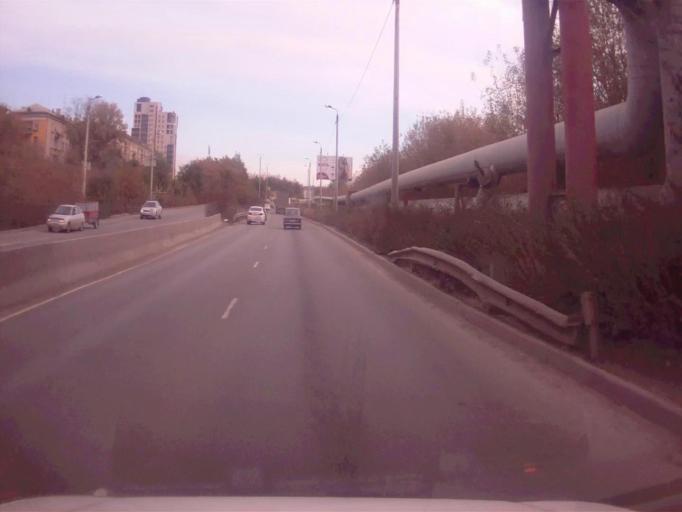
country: RU
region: Chelyabinsk
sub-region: Gorod Chelyabinsk
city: Chelyabinsk
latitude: 55.1590
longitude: 61.4334
